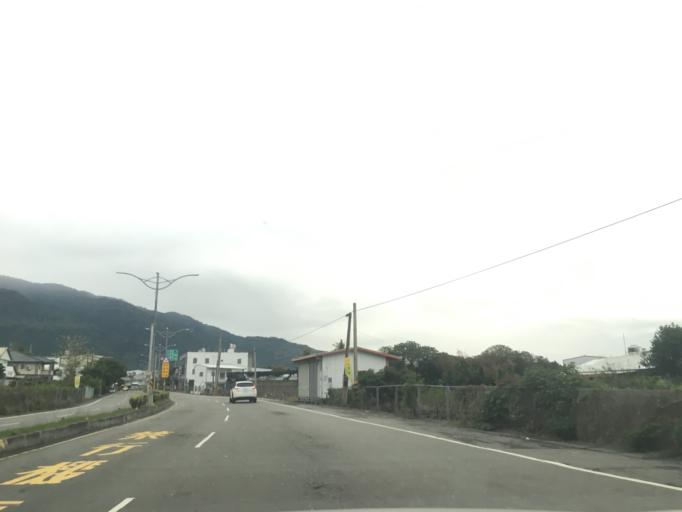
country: TW
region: Taiwan
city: Taitung City
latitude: 22.6914
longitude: 121.0465
